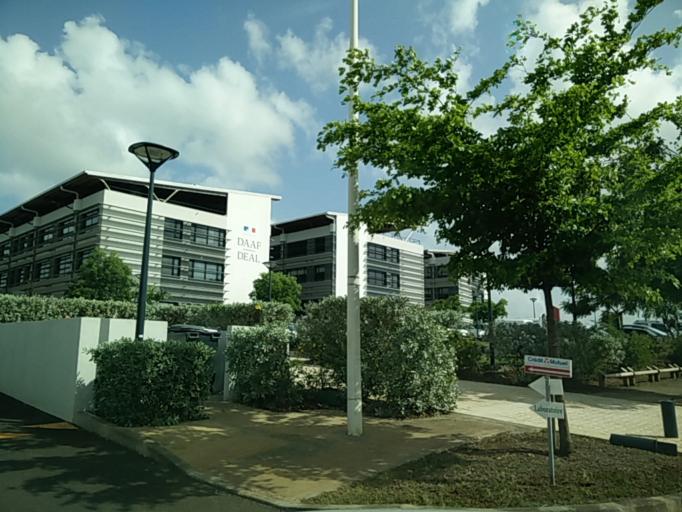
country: GP
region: Guadeloupe
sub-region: Guadeloupe
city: Les Abymes
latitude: 16.2759
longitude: -61.5100
